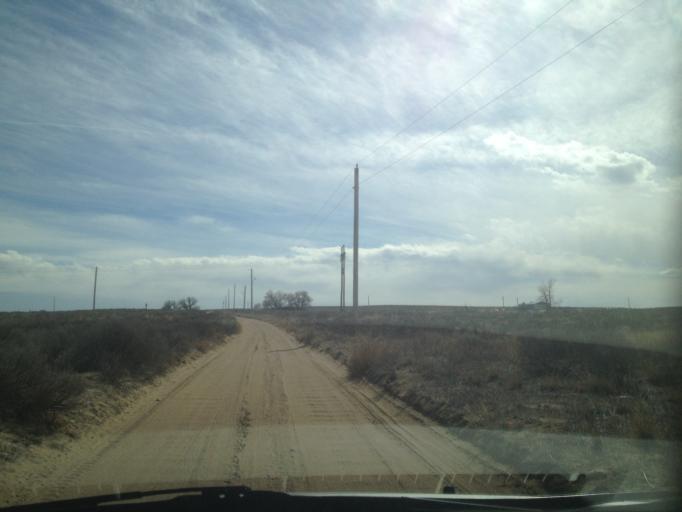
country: US
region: Colorado
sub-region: Weld County
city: Keenesburg
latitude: 40.2849
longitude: -104.2592
